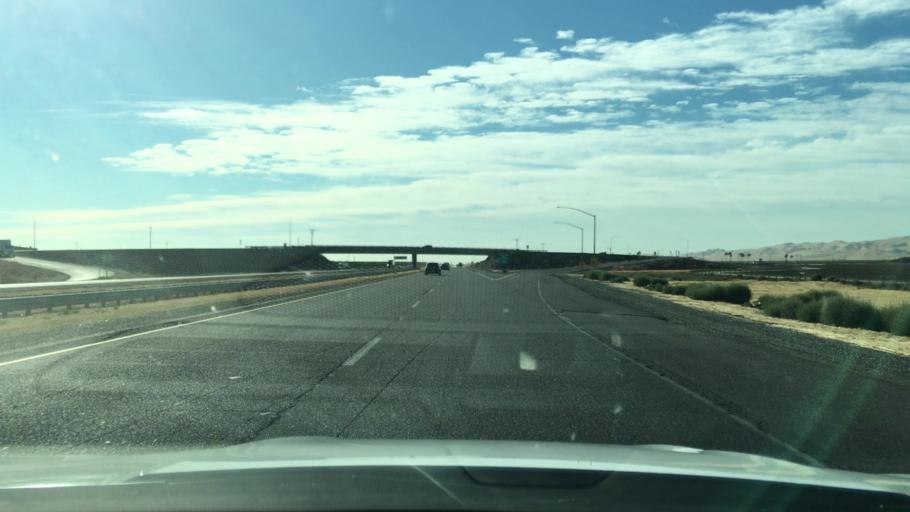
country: US
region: California
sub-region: Fresno County
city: San Joaquin
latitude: 36.4382
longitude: -120.3965
